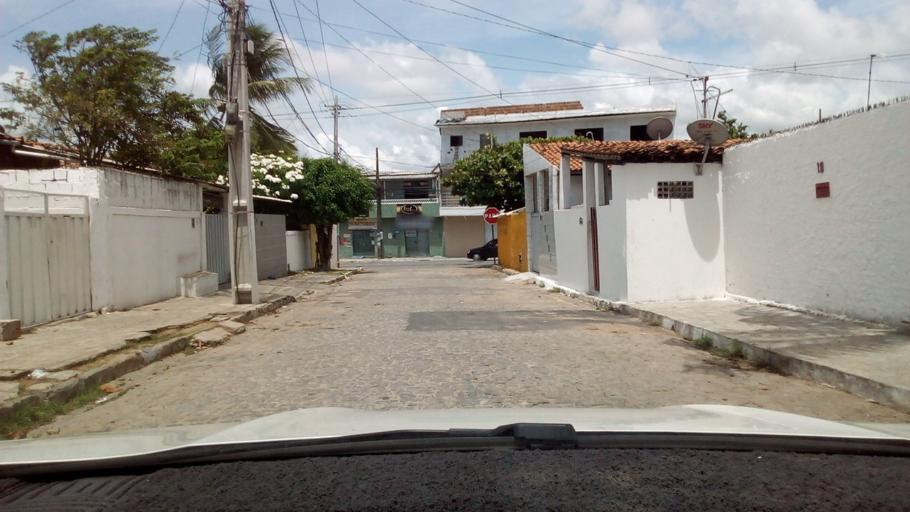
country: BR
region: Paraiba
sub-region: Joao Pessoa
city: Joao Pessoa
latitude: -7.1705
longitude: -34.8421
